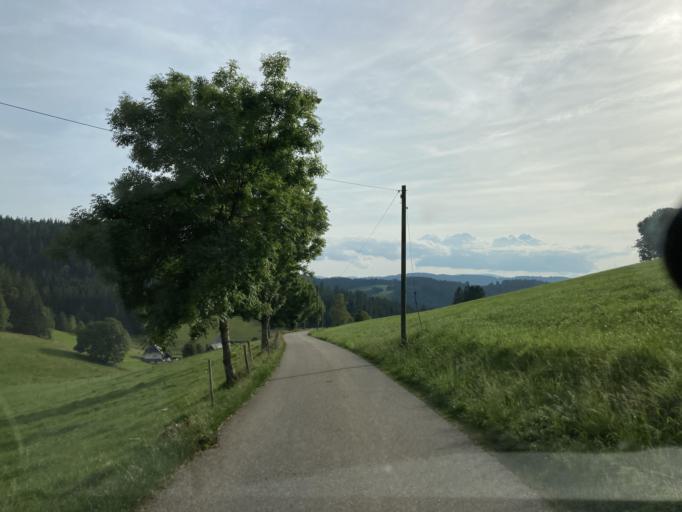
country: DE
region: Baden-Wuerttemberg
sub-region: Freiburg Region
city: Furtwangen im Schwarzwald
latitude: 47.9899
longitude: 8.1862
